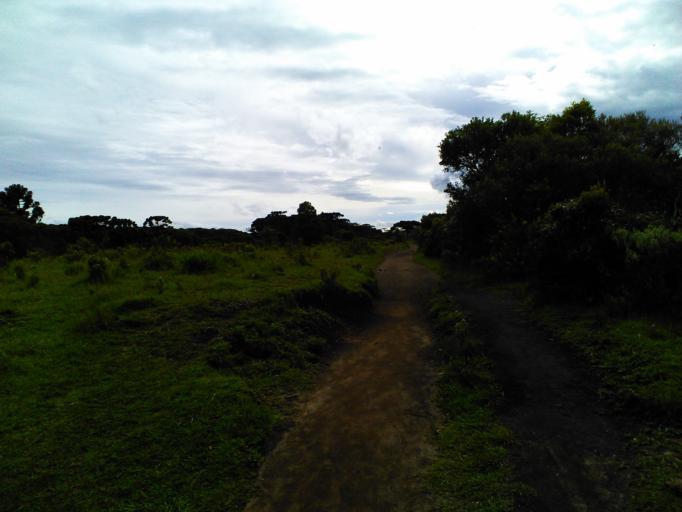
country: BR
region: Rio Grande do Sul
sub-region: Torres
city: Torres
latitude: -29.1597
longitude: -50.0771
